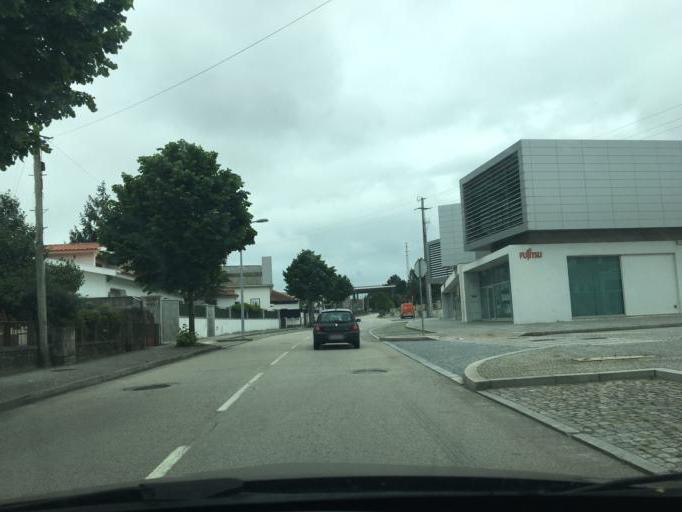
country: PT
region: Porto
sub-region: Matosinhos
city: Santa Cruz do Bispo
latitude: 41.2324
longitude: -8.6634
